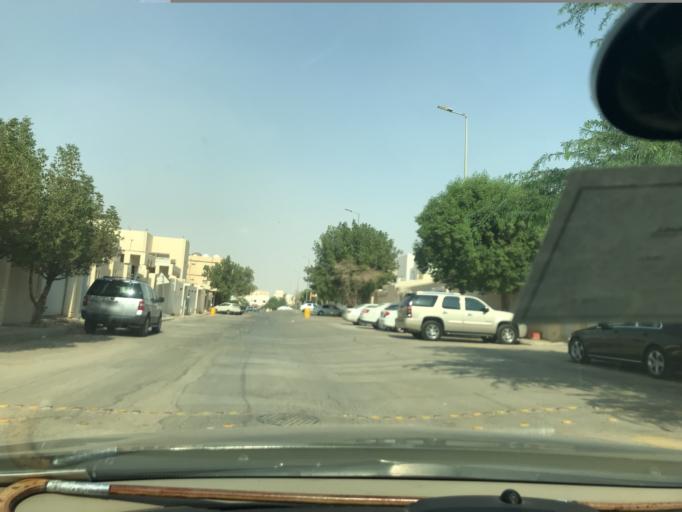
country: SA
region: Ar Riyad
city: Riyadh
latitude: 24.7434
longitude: 46.7620
